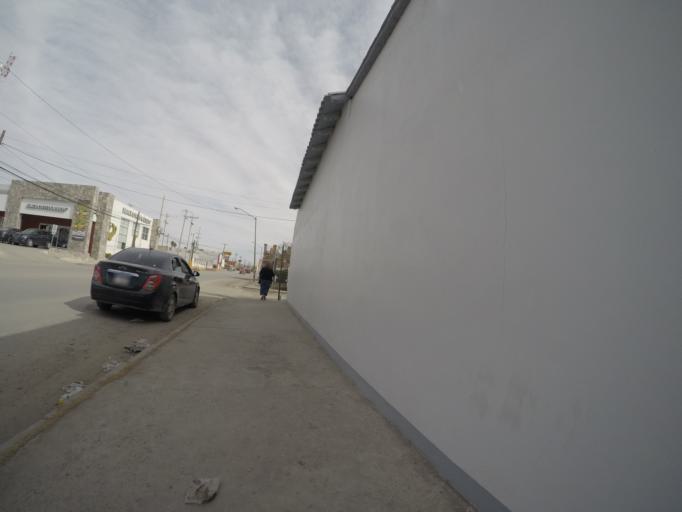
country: MX
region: Chihuahua
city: Ciudad Juarez
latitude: 31.7209
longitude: -106.4304
